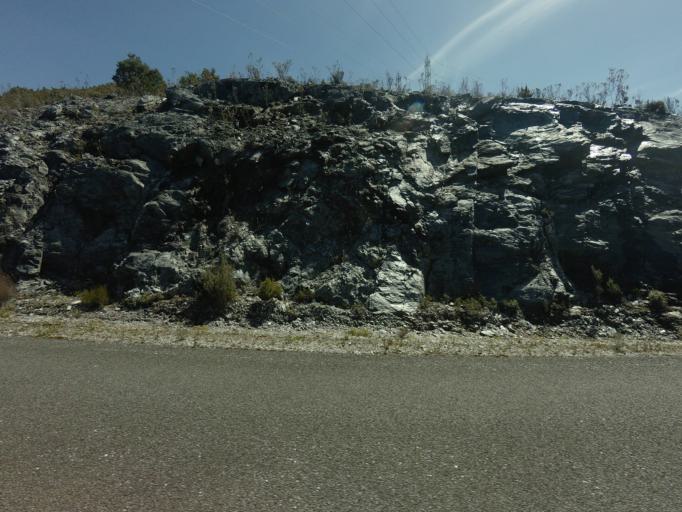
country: AU
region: Tasmania
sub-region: West Coast
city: Queenstown
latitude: -42.7479
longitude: 145.9811
